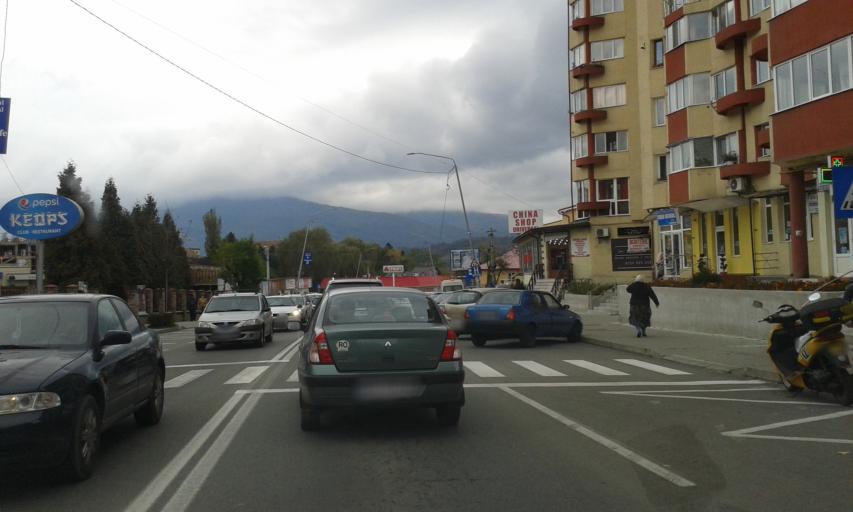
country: RO
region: Hunedoara
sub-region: Municipiul Petrosani
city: Petrosani
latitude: 45.4099
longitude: 23.3759
